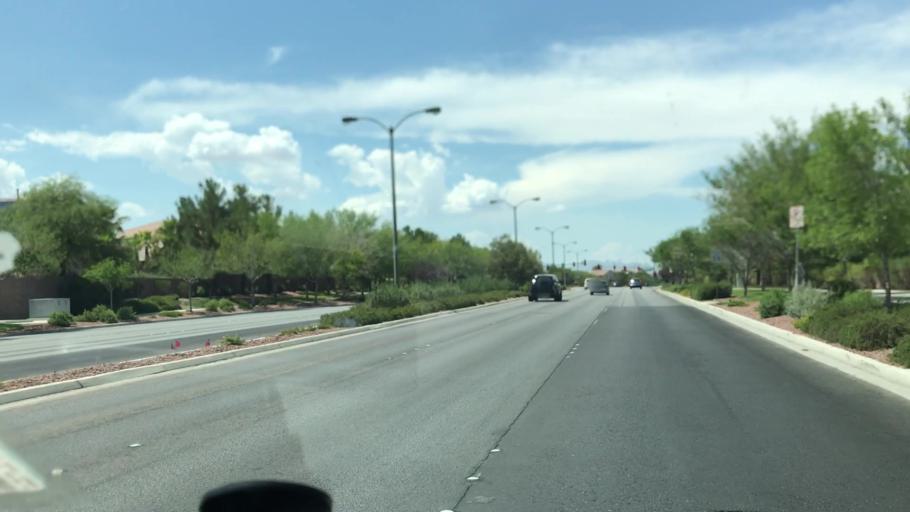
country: US
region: Nevada
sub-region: Clark County
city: Enterprise
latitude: 35.9924
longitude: -115.2054
